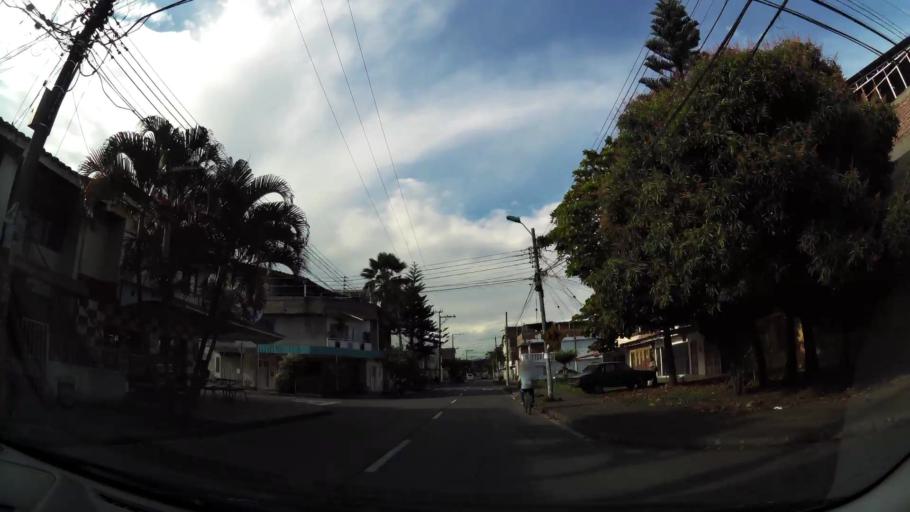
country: CO
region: Valle del Cauca
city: Cali
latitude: 3.4240
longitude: -76.5243
